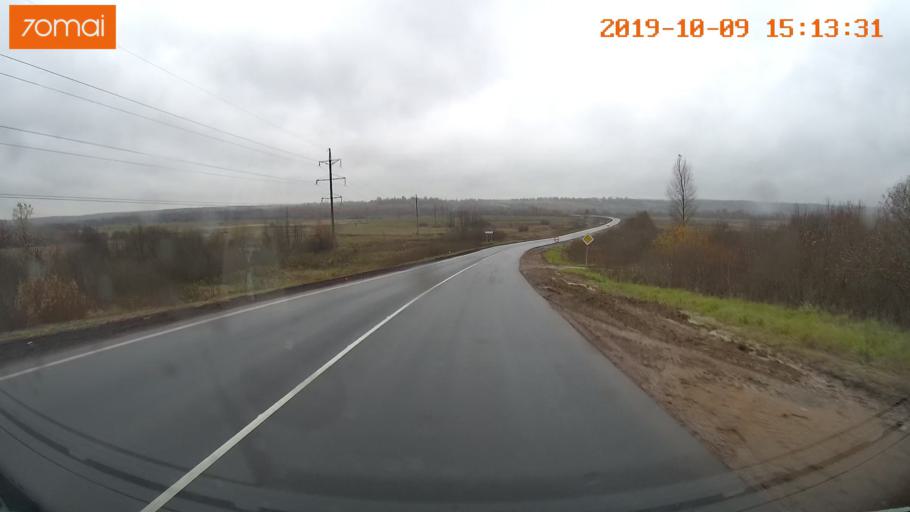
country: RU
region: Kostroma
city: Susanino
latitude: 58.1453
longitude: 41.6151
